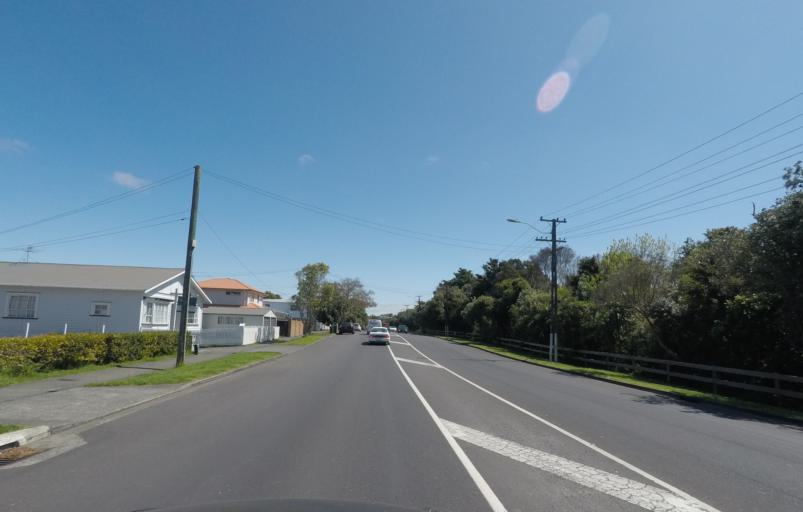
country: NZ
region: Auckland
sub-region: Auckland
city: Tamaki
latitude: -36.8870
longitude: 174.8241
